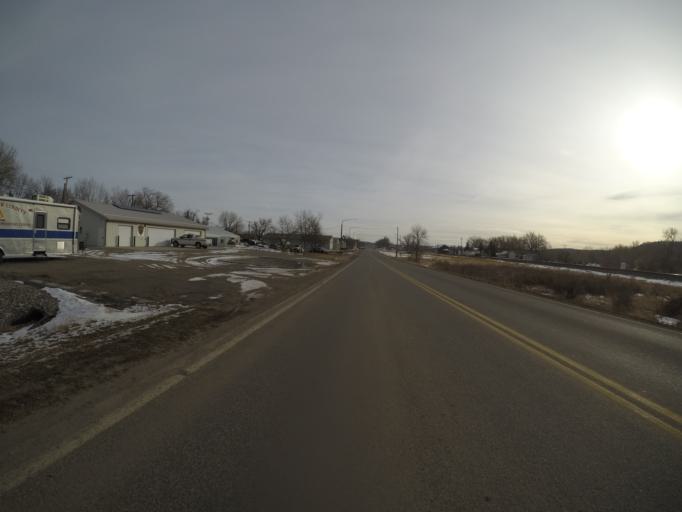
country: US
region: Montana
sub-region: Stillwater County
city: Columbus
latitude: 45.6384
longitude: -109.2591
